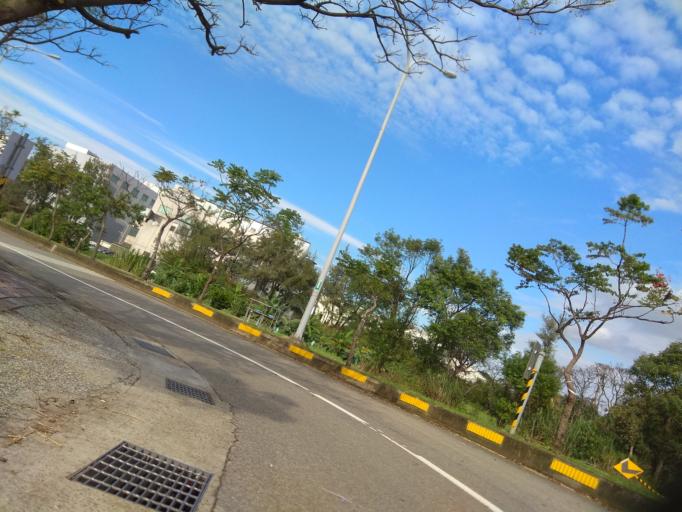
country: TW
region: Taiwan
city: Taoyuan City
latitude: 25.0550
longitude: 121.1814
